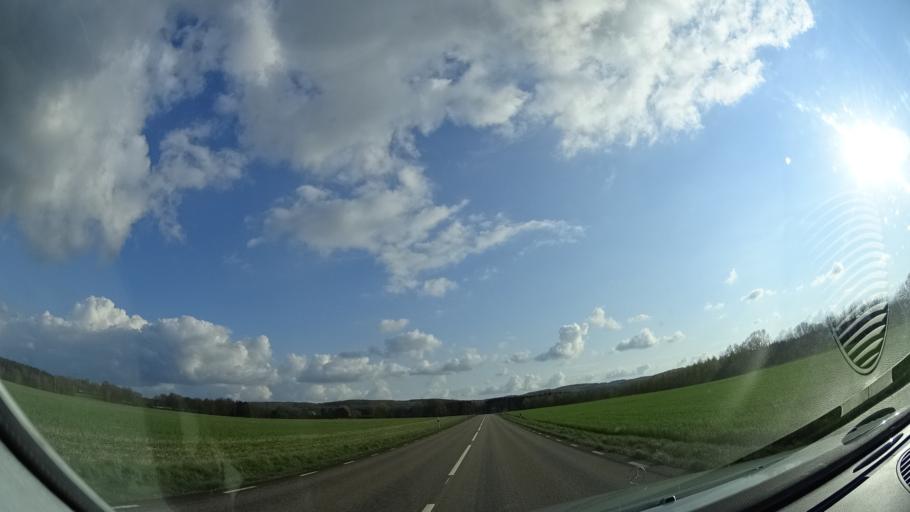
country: SE
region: Skane
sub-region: Klippans Kommun
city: Ljungbyhed
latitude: 56.0645
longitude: 13.2501
